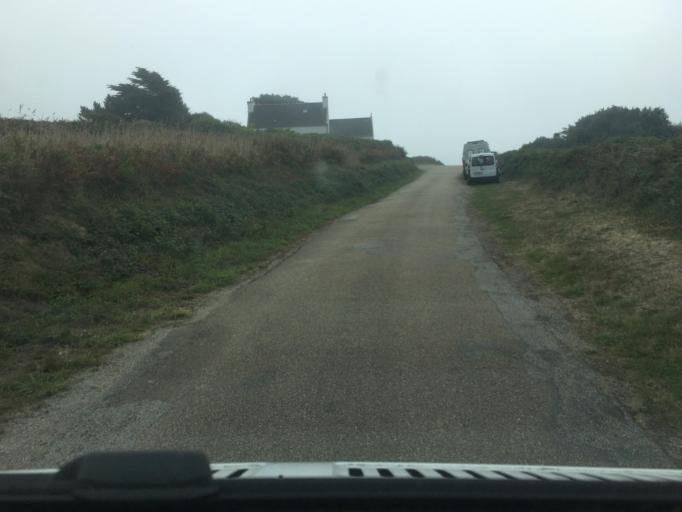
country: FR
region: Brittany
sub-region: Departement du Finistere
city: Plogoff
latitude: 48.0302
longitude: -4.6962
